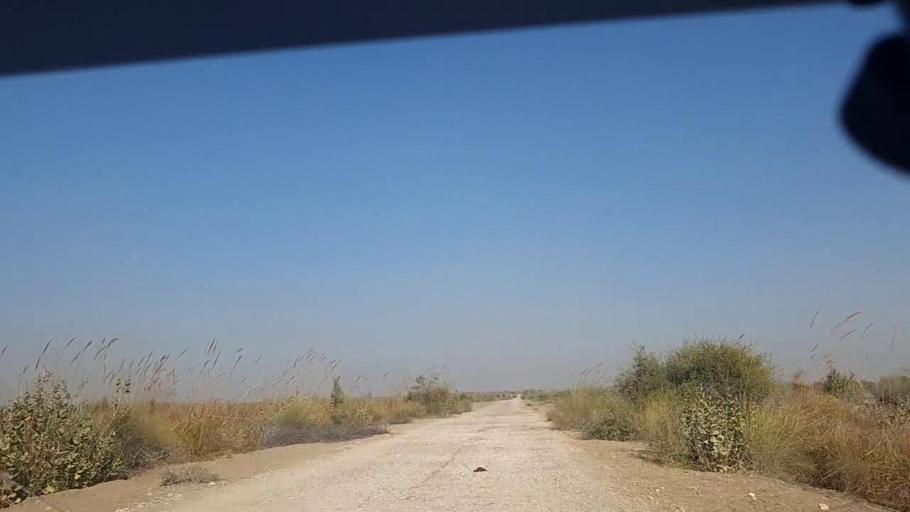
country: PK
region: Sindh
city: Khanpur
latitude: 27.5689
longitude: 69.3426
